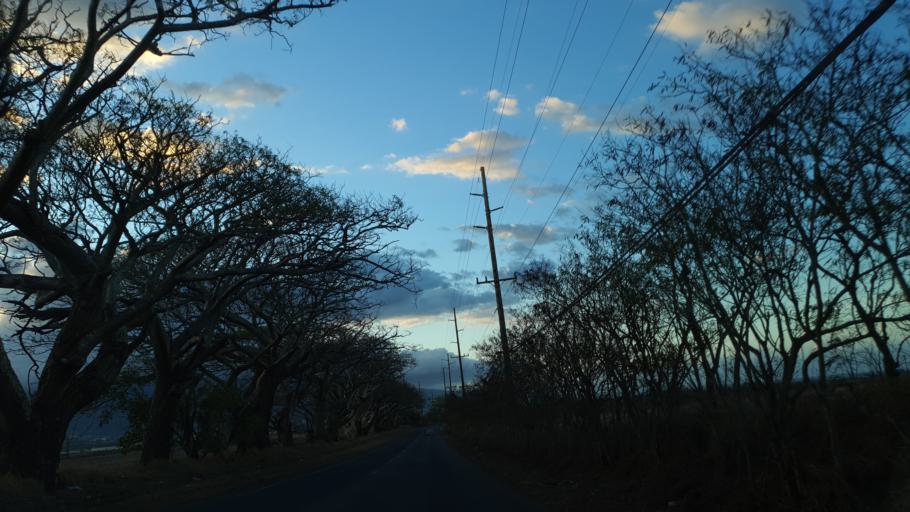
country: US
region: Hawaii
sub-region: Maui County
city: Kahului
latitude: 20.8661
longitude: -156.4327
